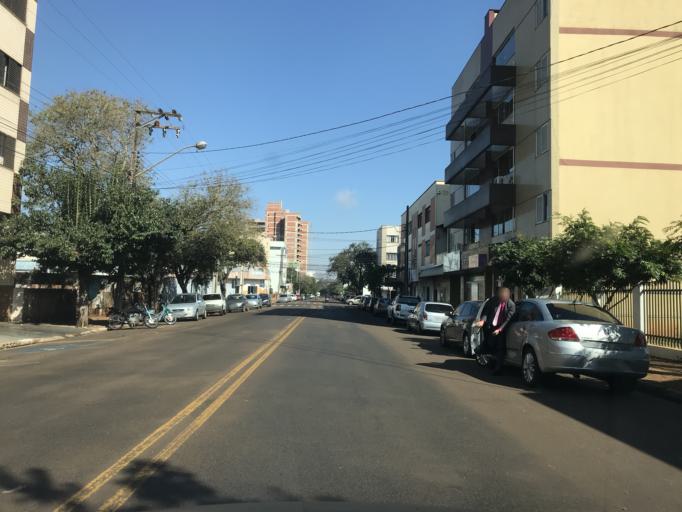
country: BR
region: Parana
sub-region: Toledo
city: Toledo
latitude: -24.7238
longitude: -53.7376
